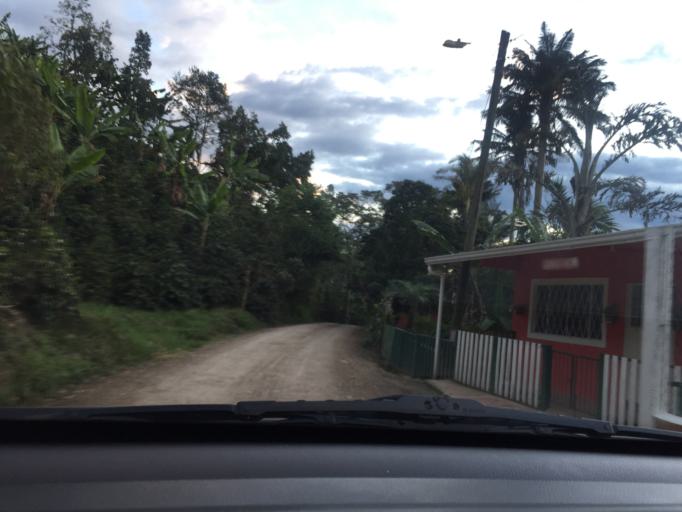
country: CO
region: Cundinamarca
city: Zipacon
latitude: 4.7000
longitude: -74.4091
